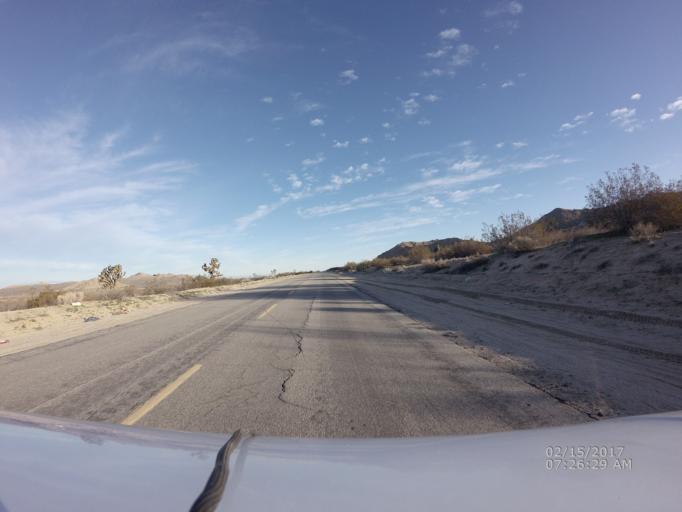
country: US
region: California
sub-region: Los Angeles County
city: Lake Los Angeles
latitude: 34.5977
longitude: -117.8714
